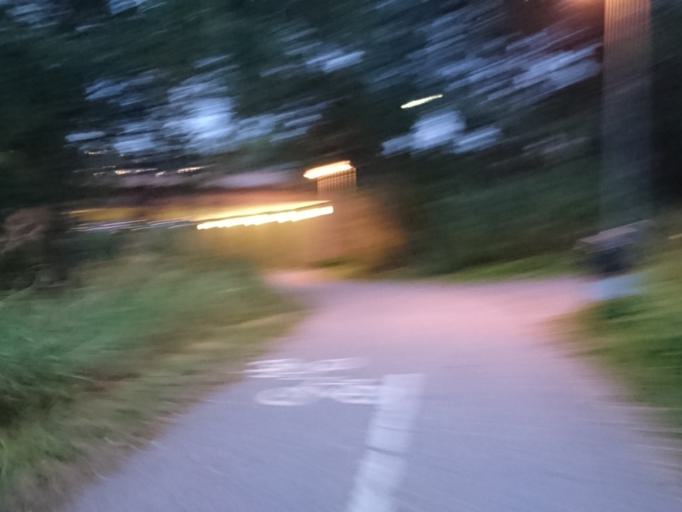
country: SE
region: Stockholm
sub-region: Stockholms Kommun
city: Arsta
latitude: 59.2808
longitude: 18.0218
